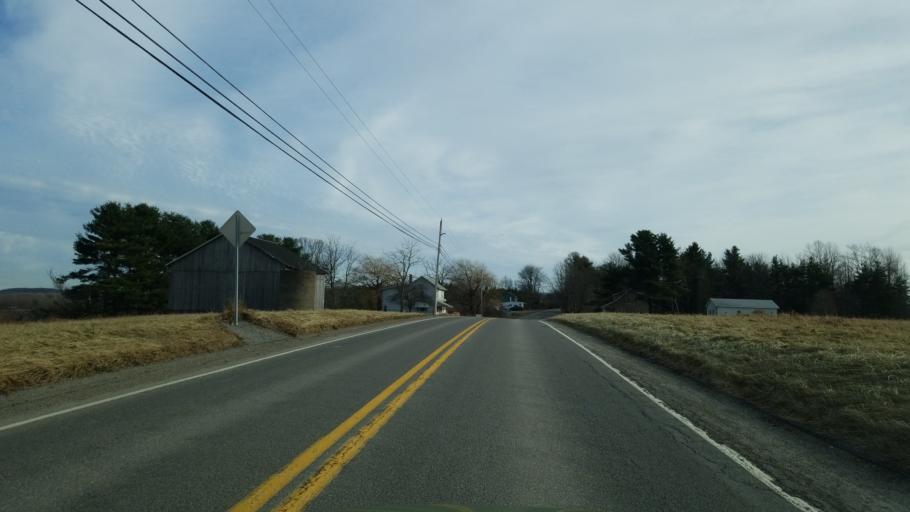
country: US
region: Pennsylvania
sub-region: Indiana County
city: Johnsonburg
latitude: 40.9157
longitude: -78.8335
